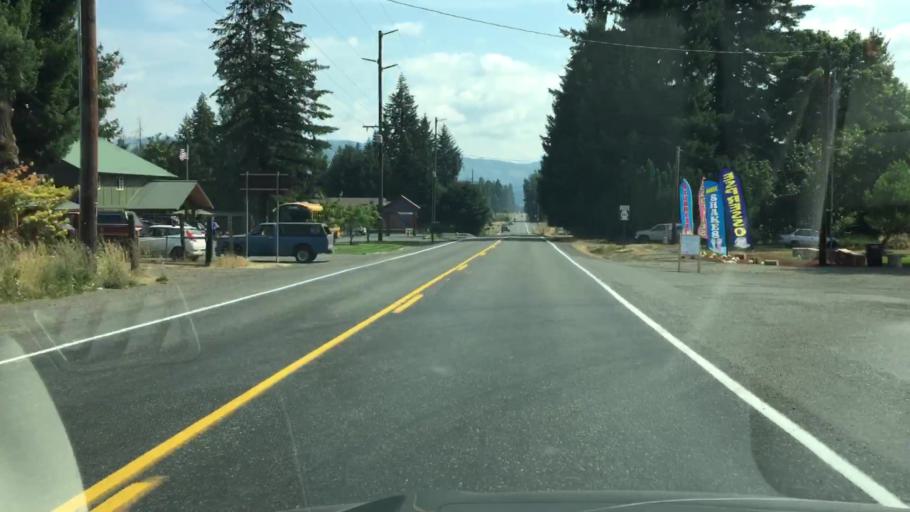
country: US
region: Washington
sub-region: Klickitat County
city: White Salmon
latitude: 45.8494
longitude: -121.5092
